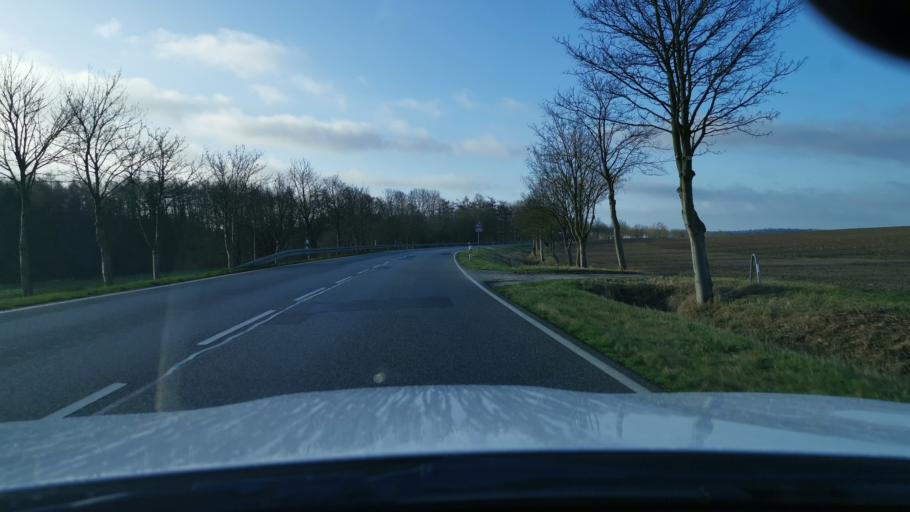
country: DE
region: Mecklenburg-Vorpommern
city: Laage
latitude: 53.9147
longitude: 12.3187
